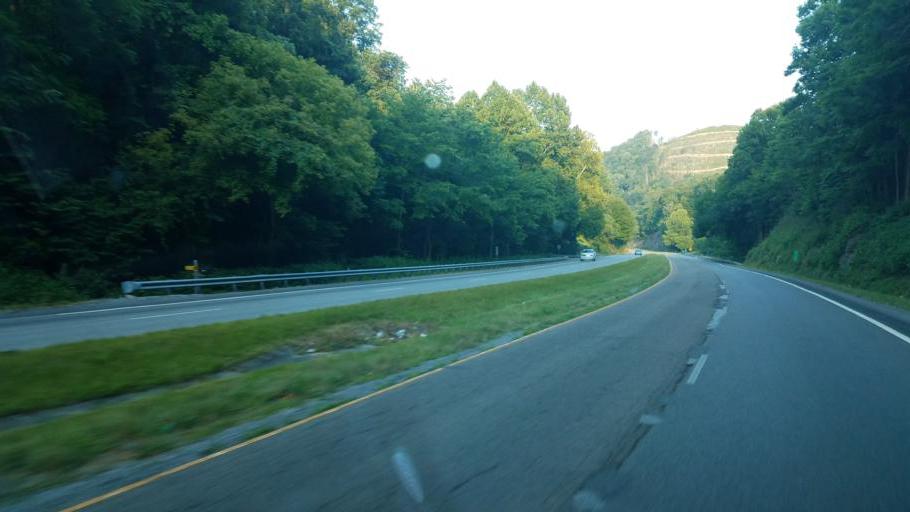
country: US
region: Virginia
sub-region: Wise County
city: Big Stone Gap
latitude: 36.7003
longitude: -82.7726
